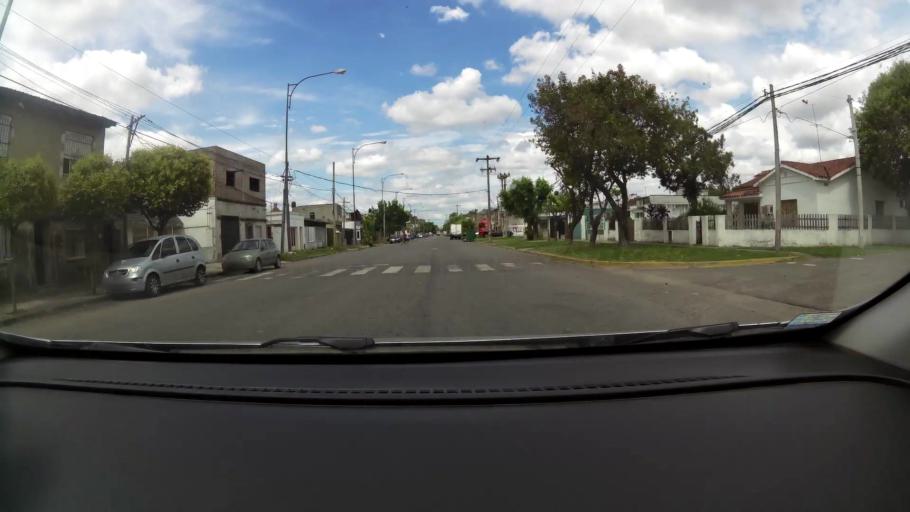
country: AR
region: Santa Fe
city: Gobernador Galvez
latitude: -33.0087
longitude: -60.6391
